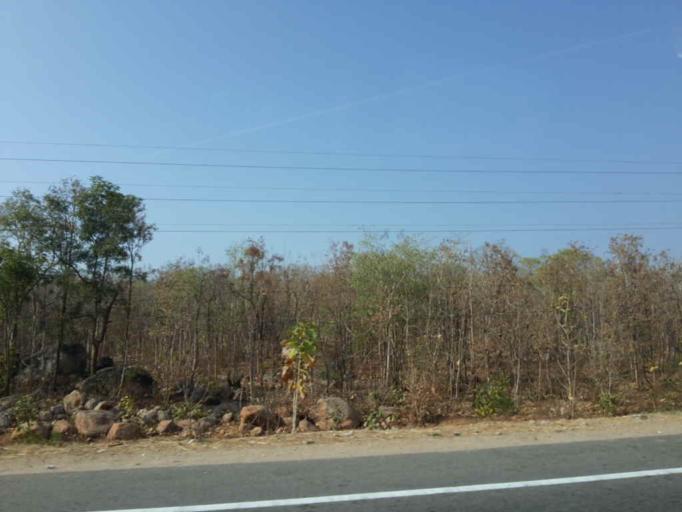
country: IN
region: Telangana
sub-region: Nizamabad District
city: Nizamabad
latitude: 18.5642
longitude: 78.2374
